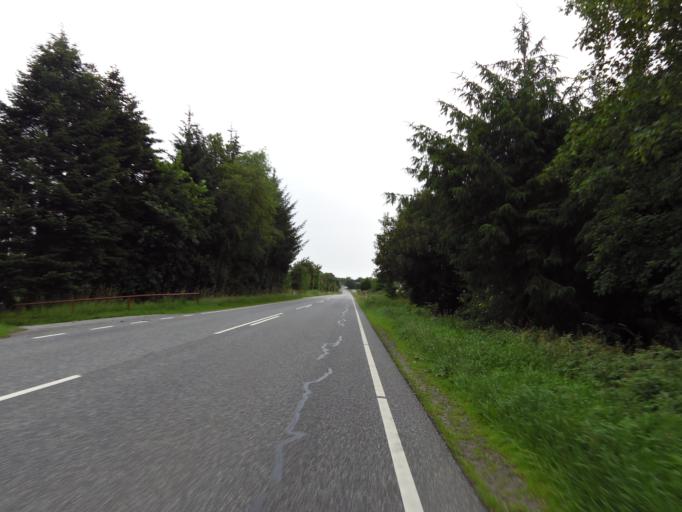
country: DK
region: South Denmark
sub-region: Tonder Kommune
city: Logumkloster
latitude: 55.1630
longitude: 8.9629
